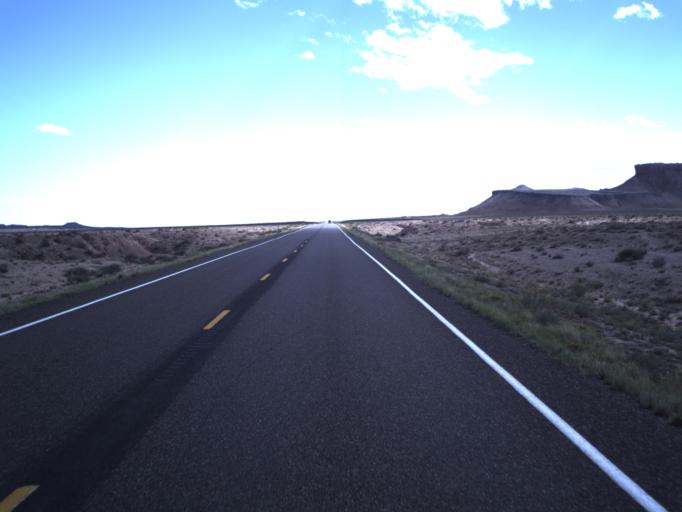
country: US
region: Utah
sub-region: Emery County
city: Ferron
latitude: 38.2940
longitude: -110.6668
